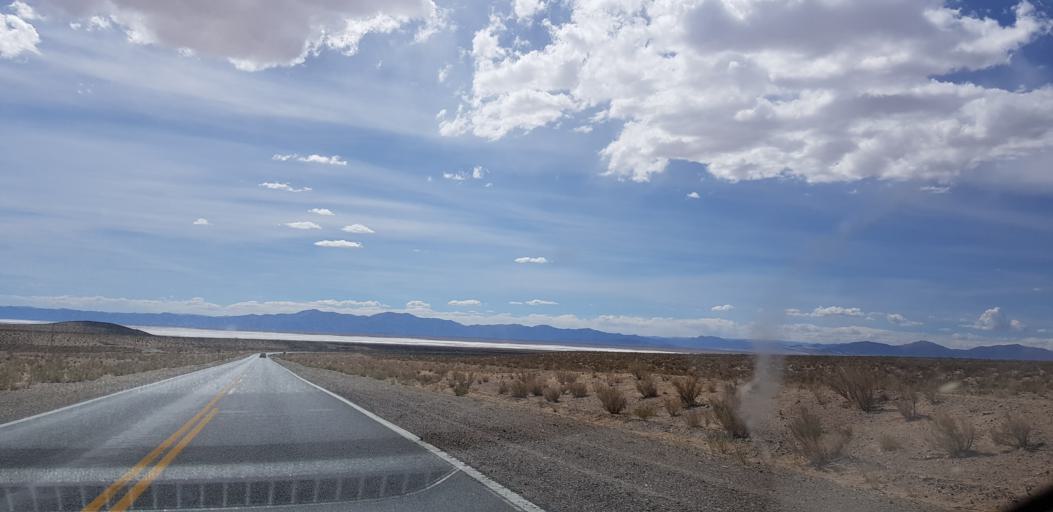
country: AR
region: Jujuy
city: Maimara
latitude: -23.6611
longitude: -65.7764
